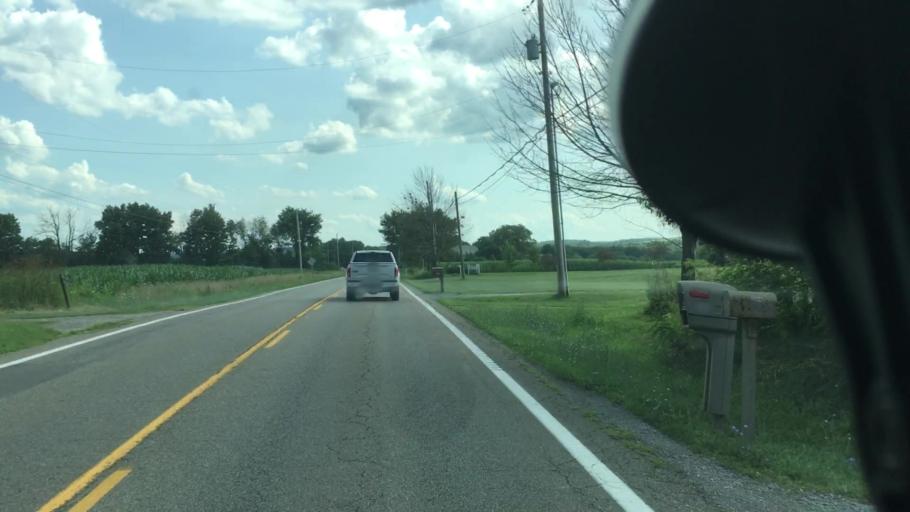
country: US
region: Ohio
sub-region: Columbiana County
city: Salem
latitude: 40.9689
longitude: -80.8290
